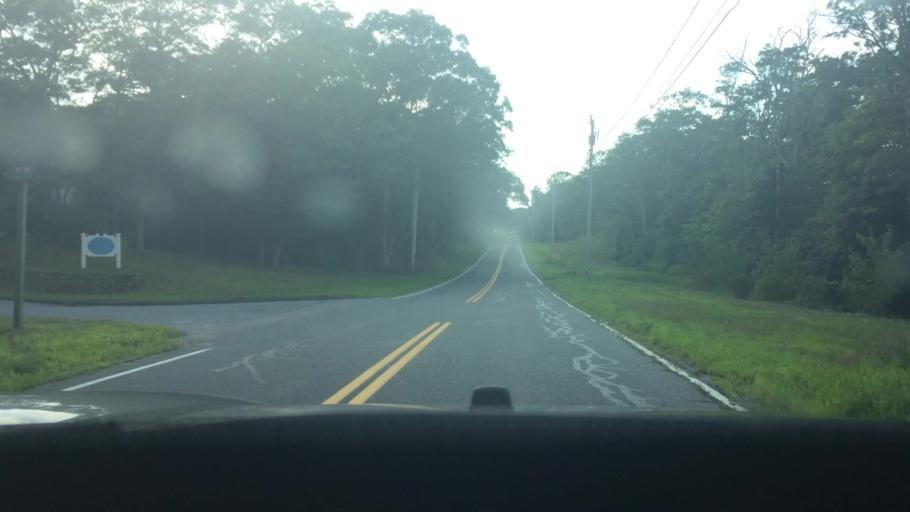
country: US
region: Massachusetts
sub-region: Barnstable County
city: Sandwich
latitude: 41.7374
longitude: -70.4797
